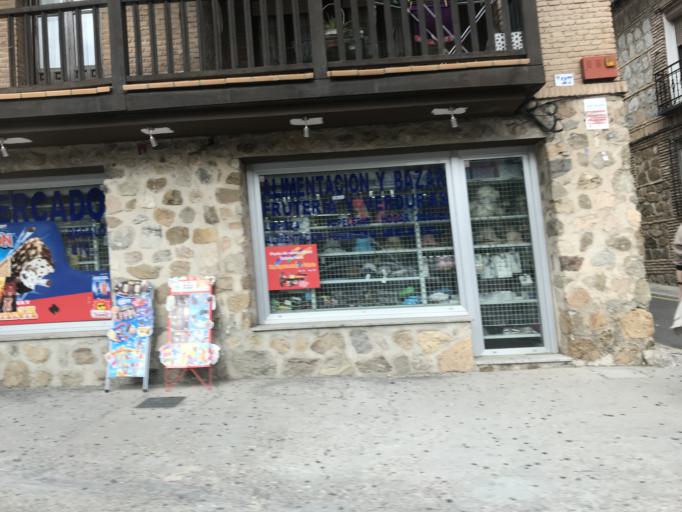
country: ES
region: Castille-La Mancha
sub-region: Province of Toledo
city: Toledo
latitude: 39.8637
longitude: -4.0218
